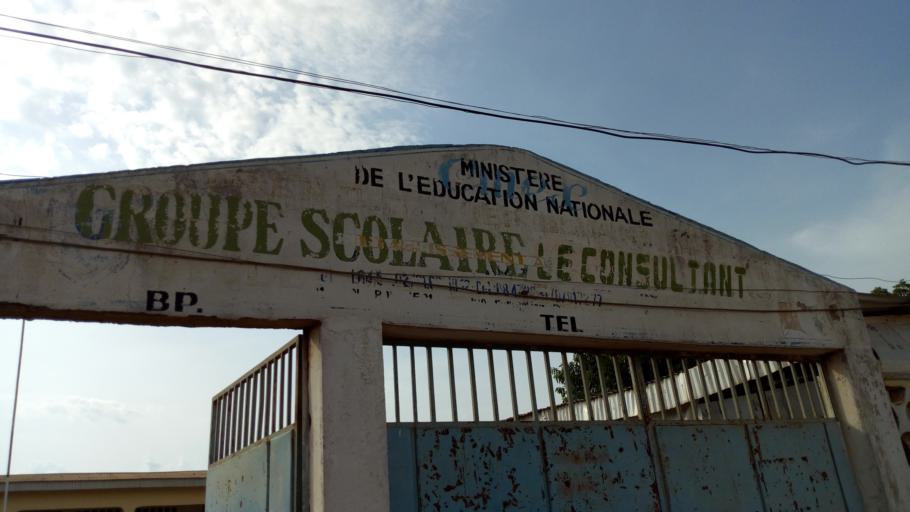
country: CI
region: Vallee du Bandama
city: Bouake
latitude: 7.7309
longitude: -5.0488
